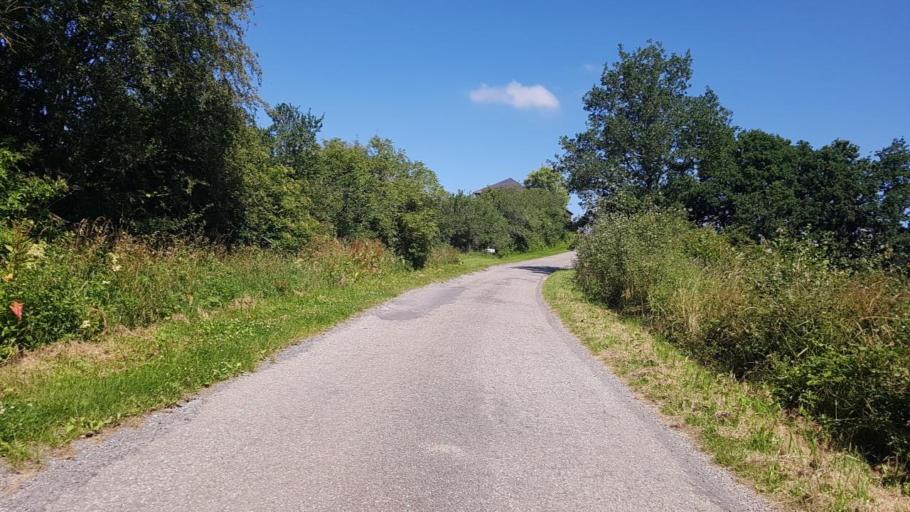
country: BE
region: Wallonia
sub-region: Province du Hainaut
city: Momignies
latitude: 50.0974
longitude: 4.2287
